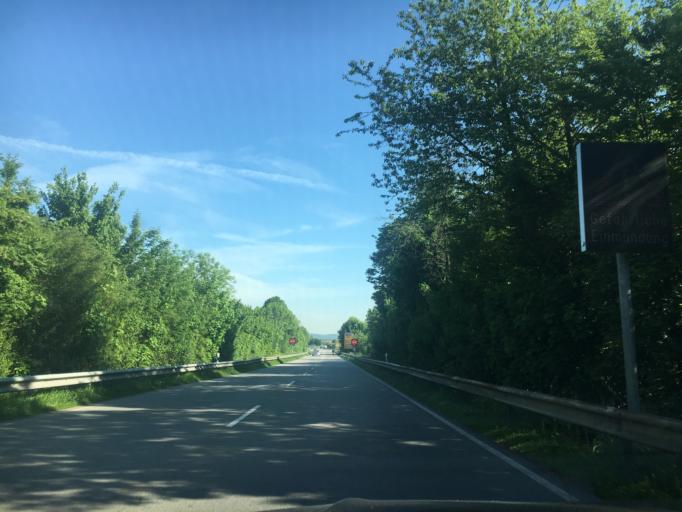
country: DE
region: Bavaria
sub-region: Upper Bavaria
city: Altoetting
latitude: 48.2233
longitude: 12.6575
